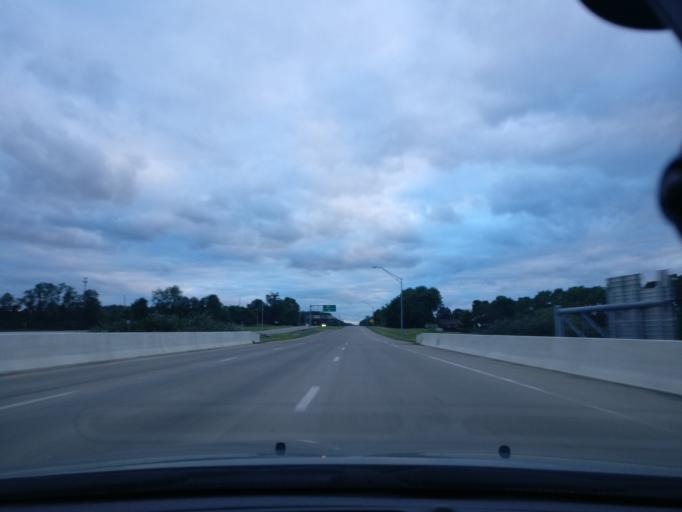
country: US
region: Ohio
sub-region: Greene County
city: Xenia
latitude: 39.6627
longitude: -83.9488
